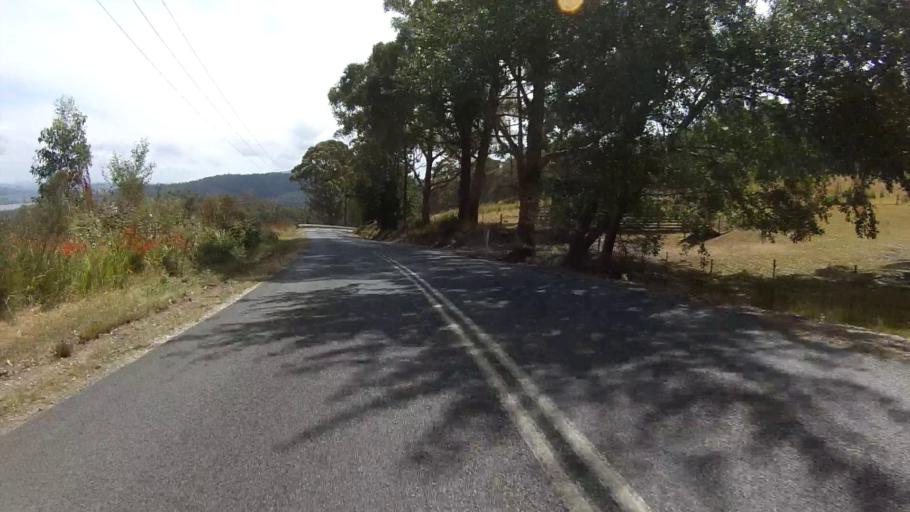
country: AU
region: Tasmania
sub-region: Huon Valley
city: Cygnet
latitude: -43.2262
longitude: 147.1278
